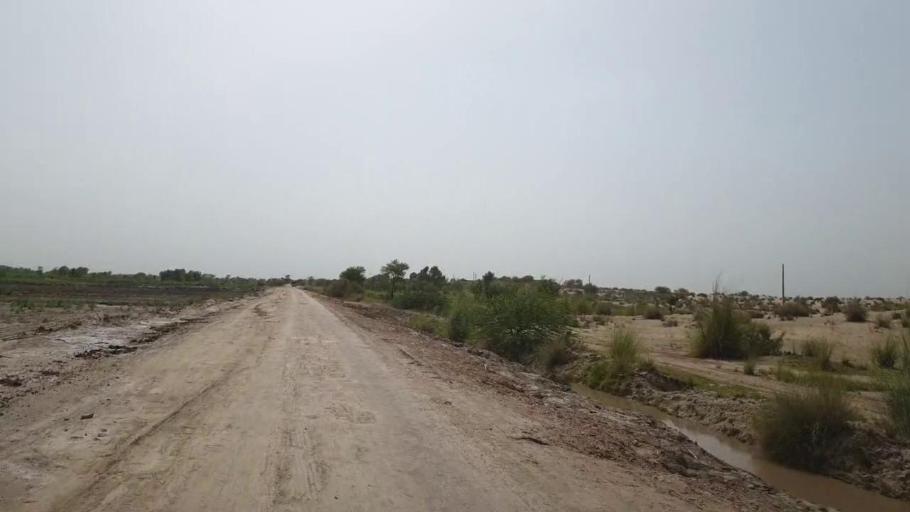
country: PK
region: Sindh
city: Bandhi
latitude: 26.5386
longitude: 68.3930
